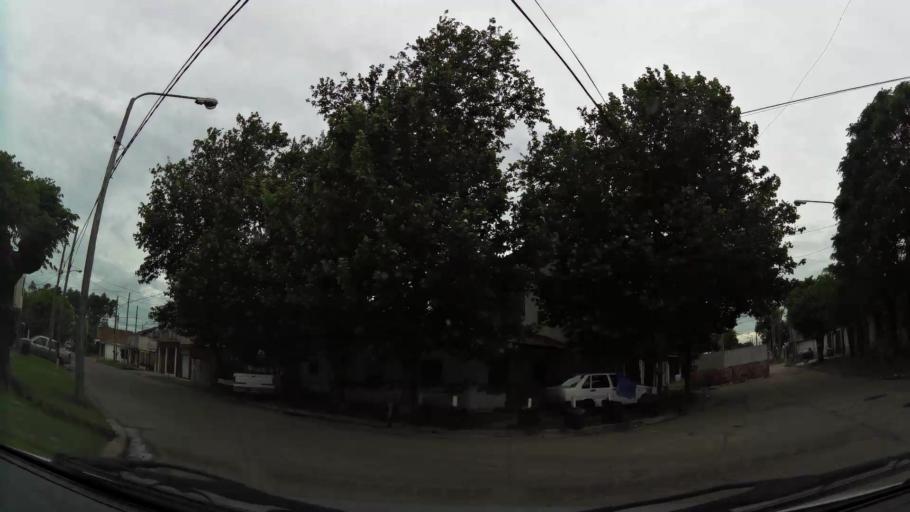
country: AR
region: Buenos Aires
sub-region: Partido de Lanus
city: Lanus
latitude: -34.7226
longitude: -58.3735
